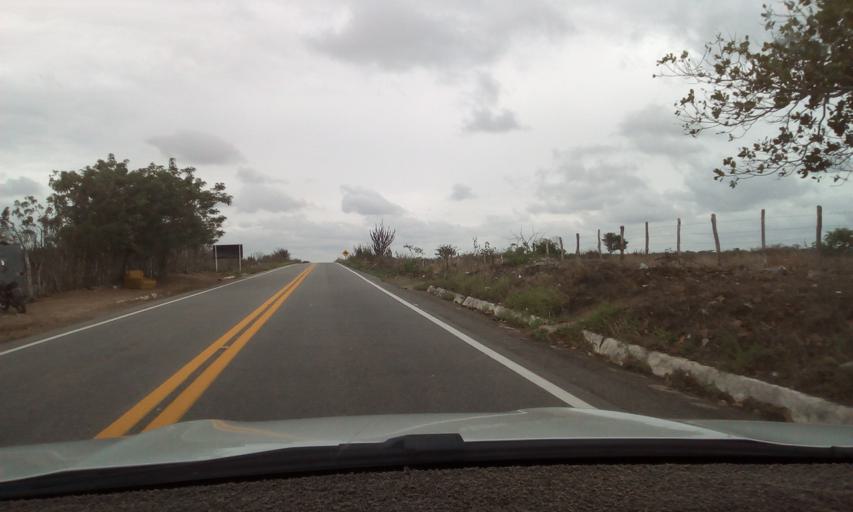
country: BR
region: Paraiba
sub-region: Areia
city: Remigio
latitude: -6.9182
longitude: -35.8511
